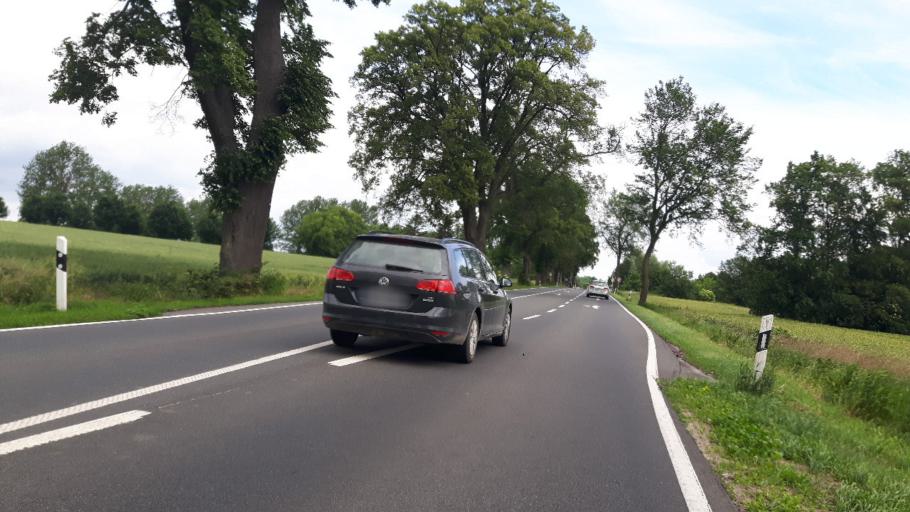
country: PL
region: West Pomeranian Voivodeship
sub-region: Powiat policki
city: Kolbaskowo
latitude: 53.3044
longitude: 14.4079
